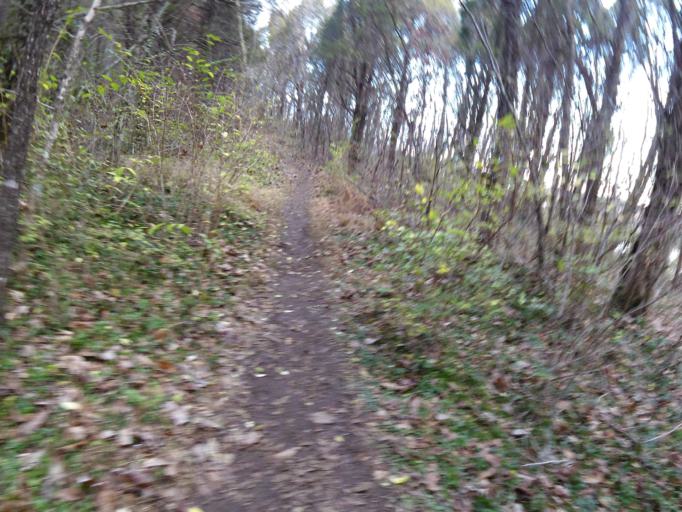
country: US
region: Tennessee
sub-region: Knox County
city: Knoxville
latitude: 35.9469
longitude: -83.8470
